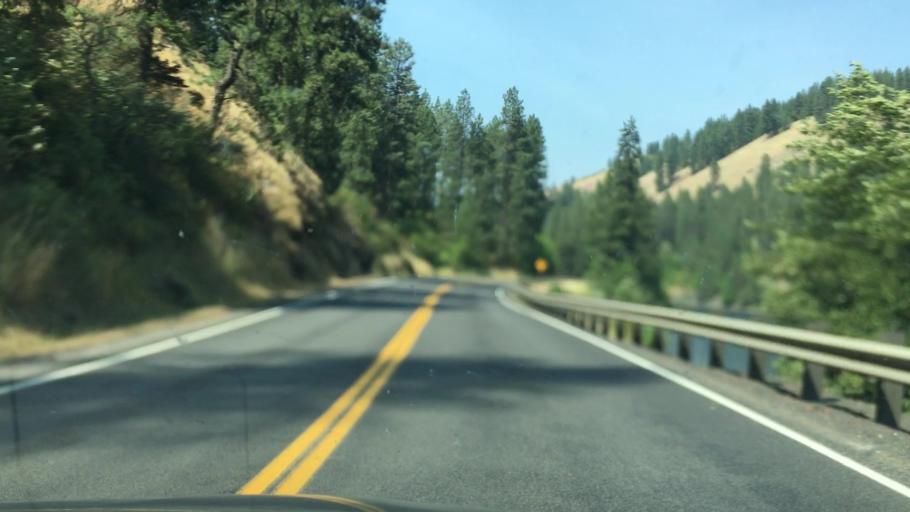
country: US
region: Idaho
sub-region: Clearwater County
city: Orofino
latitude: 46.5001
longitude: -116.3878
